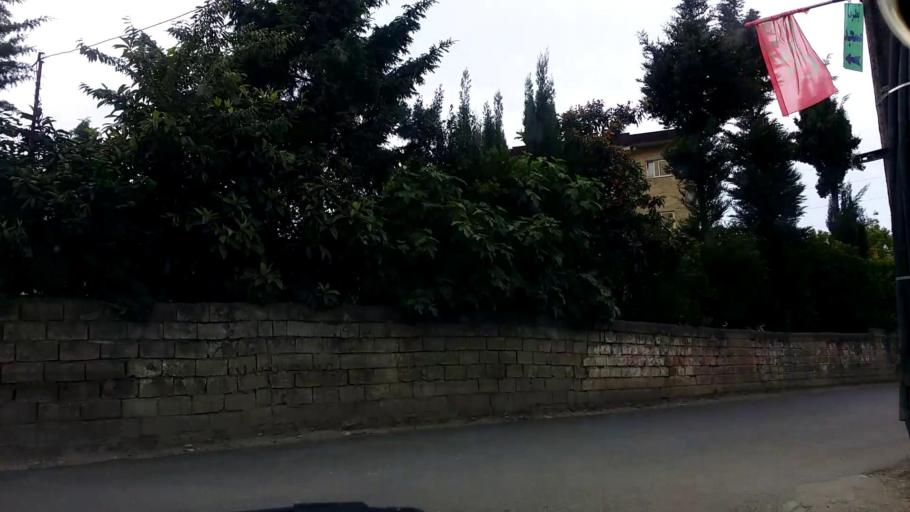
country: IR
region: Mazandaran
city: Chalus
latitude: 36.6588
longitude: 51.4052
